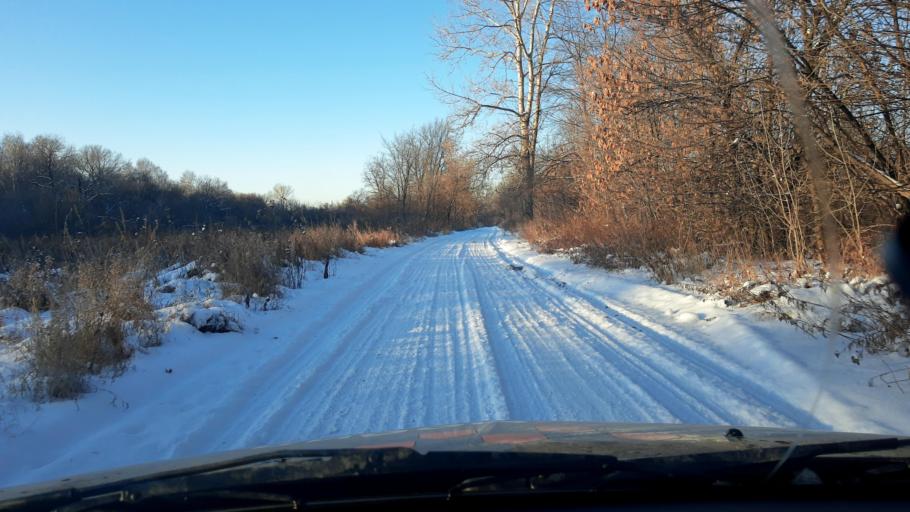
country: RU
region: Bashkortostan
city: Ufa
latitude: 54.6577
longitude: 55.9704
